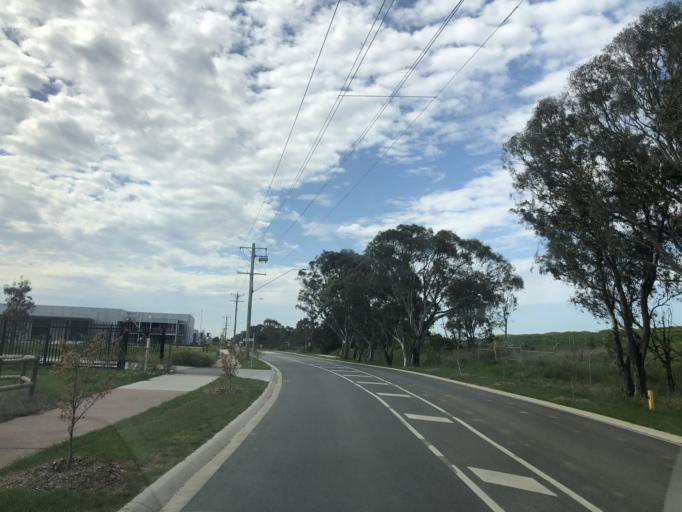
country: AU
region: Victoria
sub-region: Casey
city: Hampton Park
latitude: -38.0426
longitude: 145.2272
